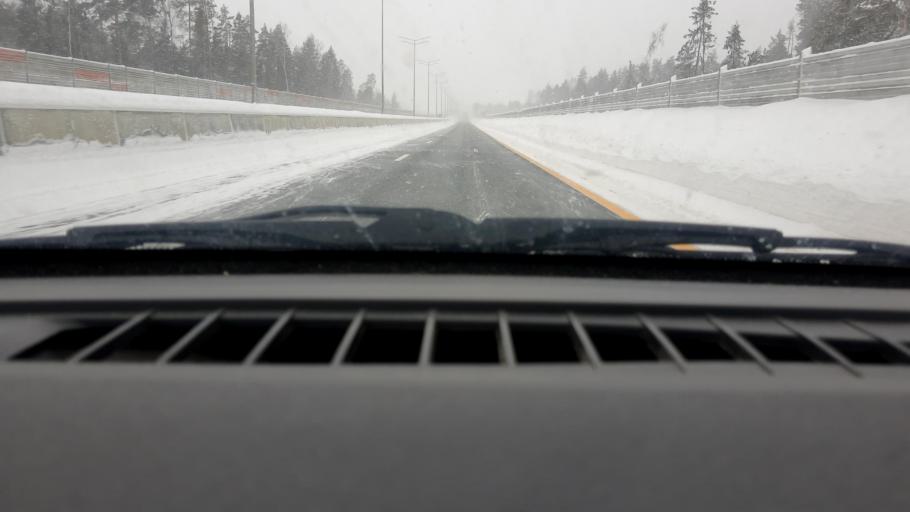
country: RU
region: Moskovskaya
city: Krasnoarmeysk
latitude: 56.0321
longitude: 38.2123
